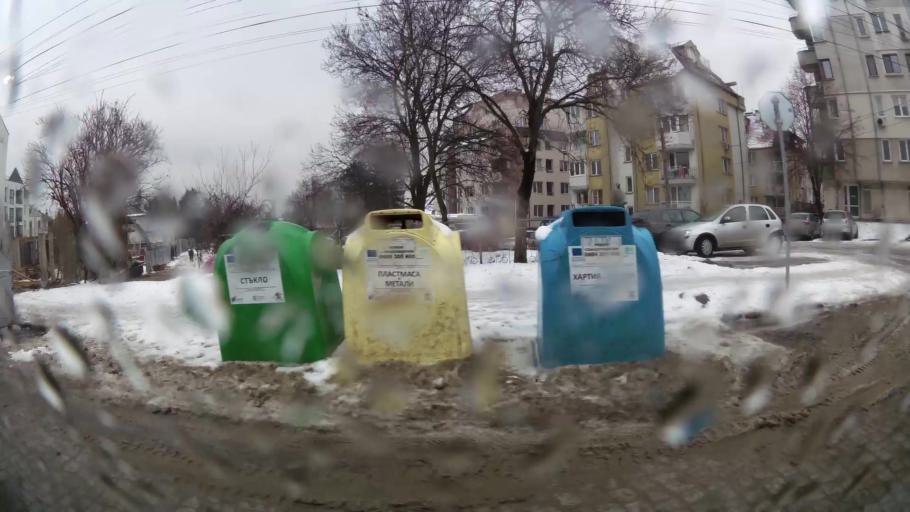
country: BG
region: Sofia-Capital
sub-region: Stolichna Obshtina
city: Sofia
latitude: 42.6735
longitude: 23.2630
